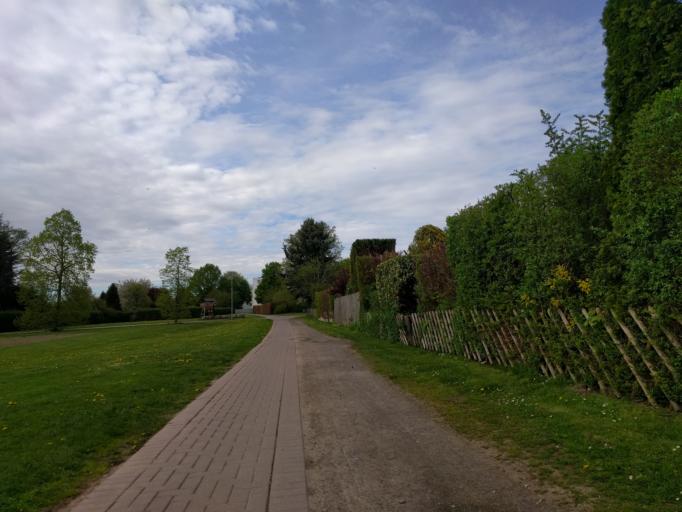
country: DE
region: North Rhine-Westphalia
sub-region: Regierungsbezirk Detmold
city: Bielefeld
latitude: 52.0529
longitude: 8.5362
